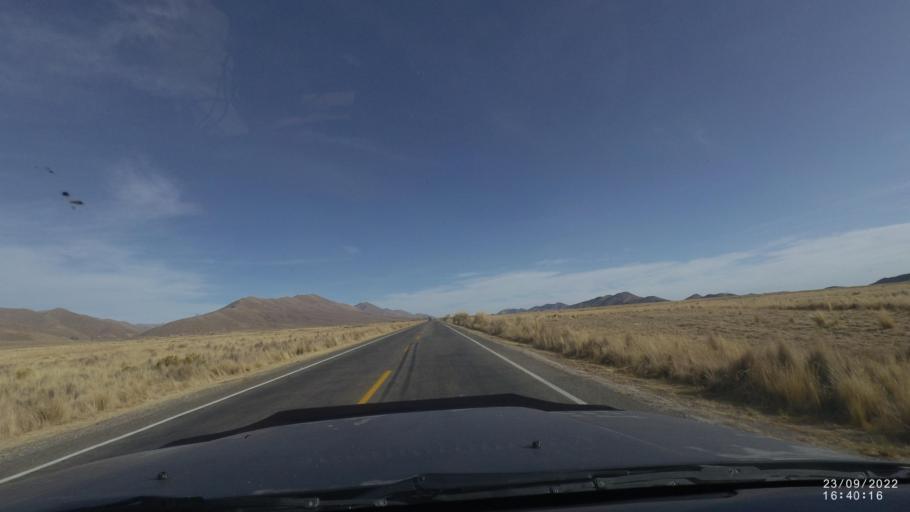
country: BO
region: Oruro
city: Machacamarca
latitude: -18.2734
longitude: -66.9969
